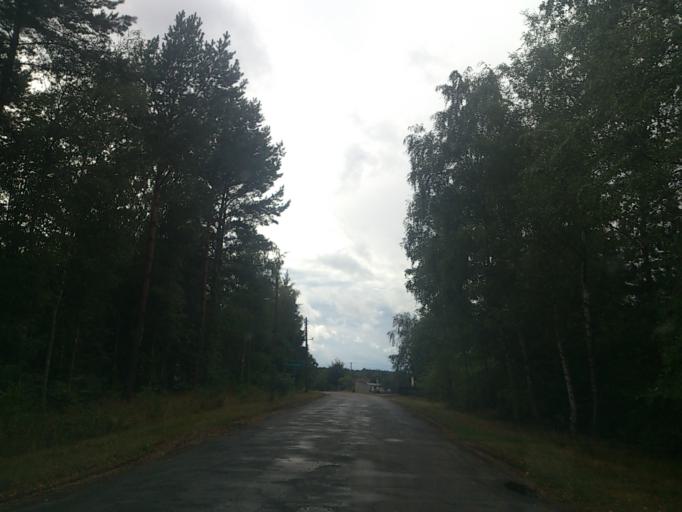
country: PL
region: Greater Poland Voivodeship
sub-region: Powiat poznanski
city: Kobylnica
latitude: 52.5194
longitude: 17.1506
